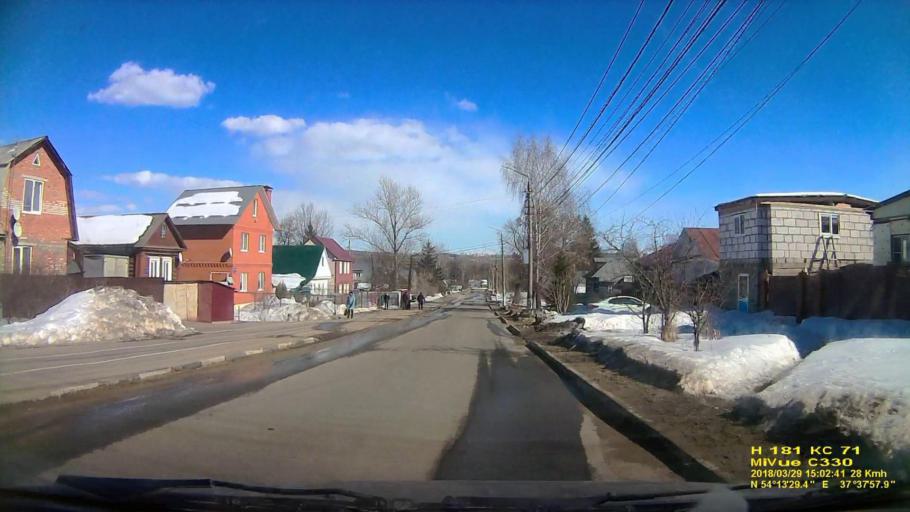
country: RU
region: Tula
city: Tula
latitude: 54.2248
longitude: 37.6328
